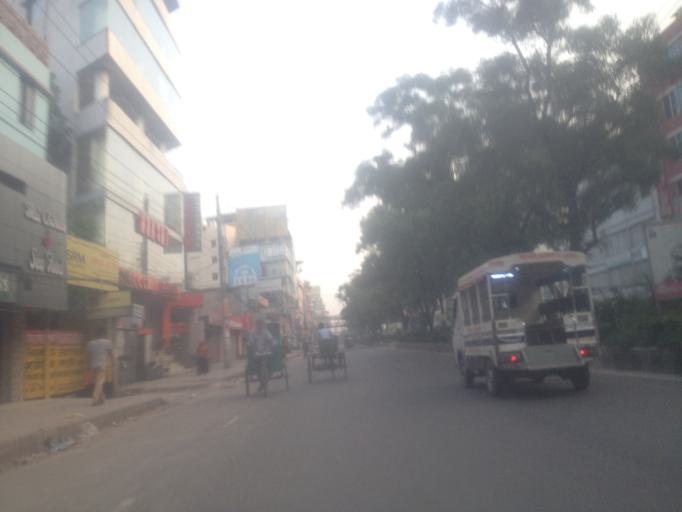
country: BD
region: Dhaka
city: Azimpur
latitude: 23.7927
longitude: 90.3747
